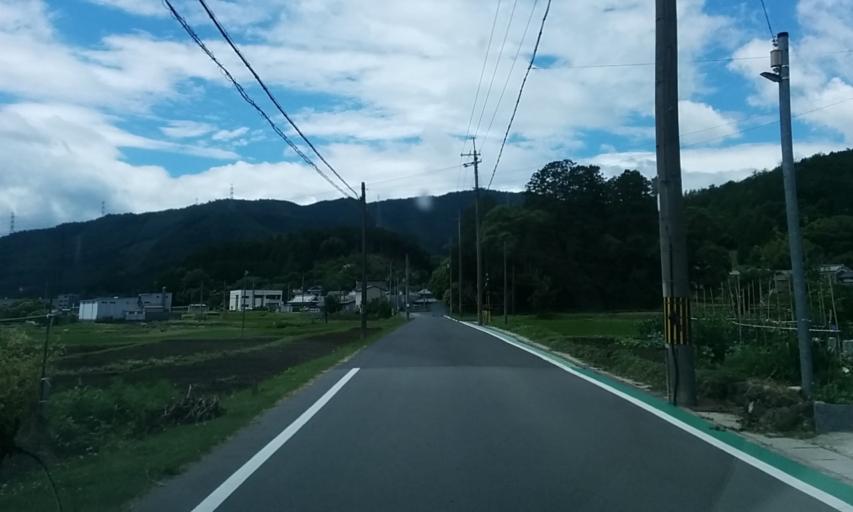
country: JP
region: Kyoto
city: Kameoka
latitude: 35.0116
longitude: 135.4839
